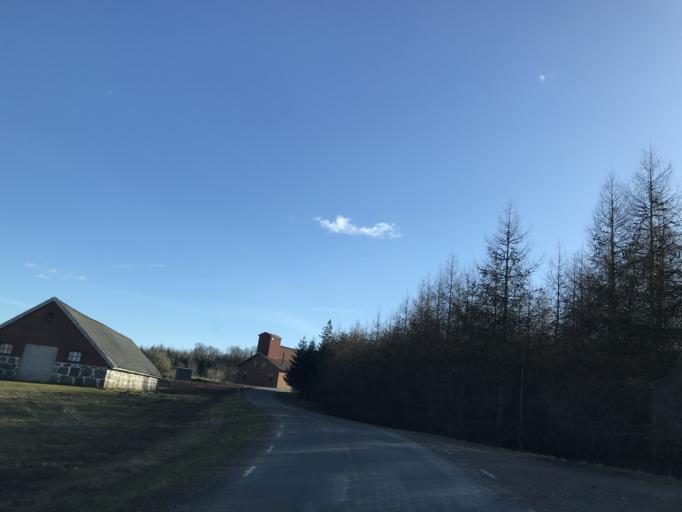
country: SE
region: Skane
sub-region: Ystads Kommun
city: Ystad
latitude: 55.5534
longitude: 13.8075
